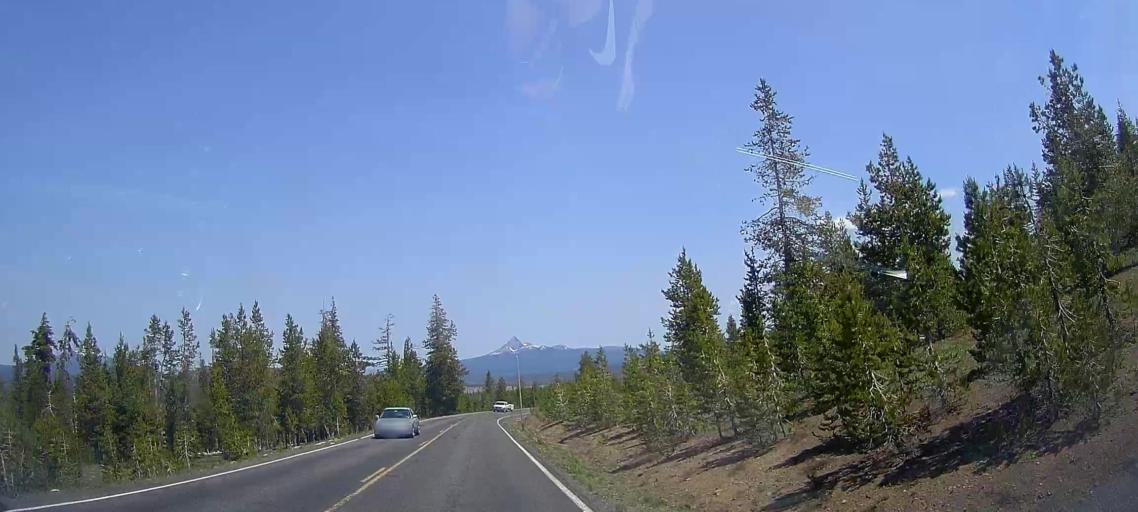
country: US
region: Oregon
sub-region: Jackson County
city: Shady Cove
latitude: 42.9907
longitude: -122.1432
